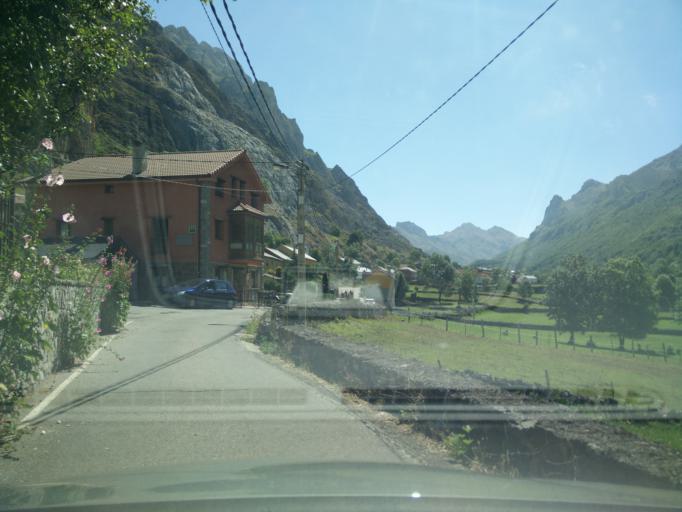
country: ES
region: Asturias
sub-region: Province of Asturias
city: Pola de Somiedo
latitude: 43.0739
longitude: -6.2040
